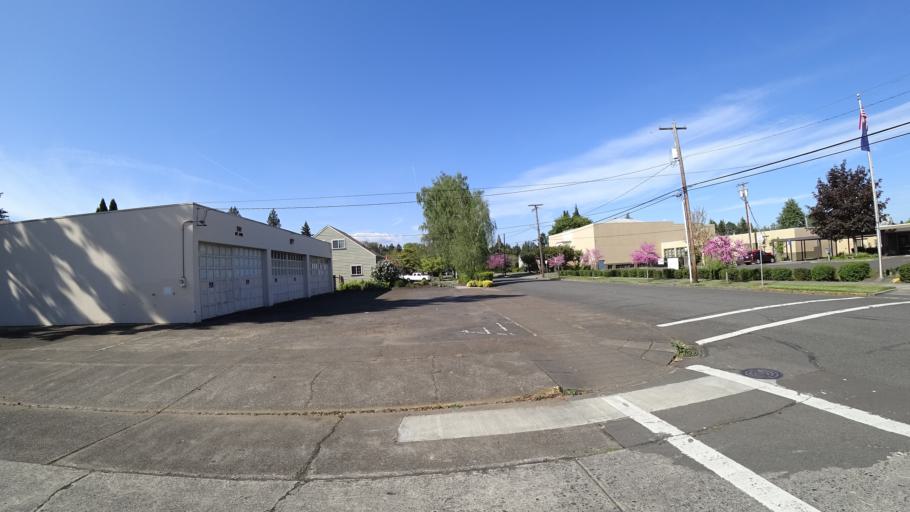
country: US
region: Oregon
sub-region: Washington County
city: Hillsboro
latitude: 45.5273
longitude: -122.9862
